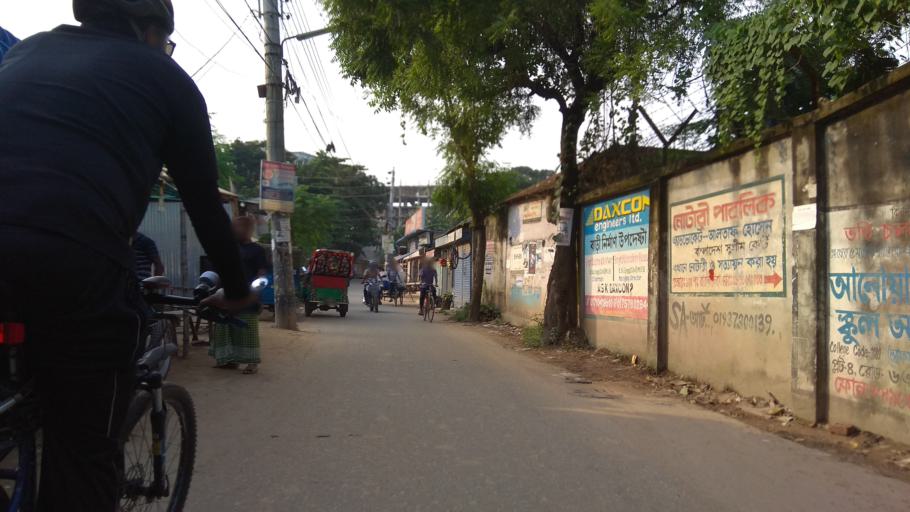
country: BD
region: Dhaka
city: Tungi
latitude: 23.8359
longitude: 90.3876
